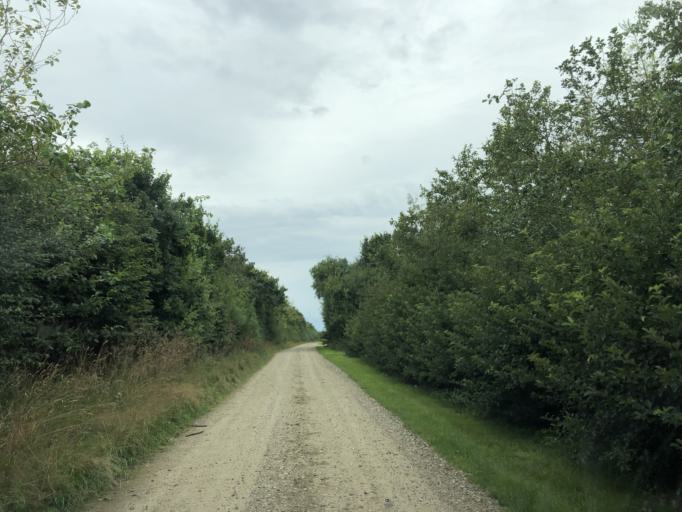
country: DK
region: Central Jutland
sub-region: Ringkobing-Skjern Kommune
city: Ringkobing
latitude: 56.1314
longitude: 8.2516
